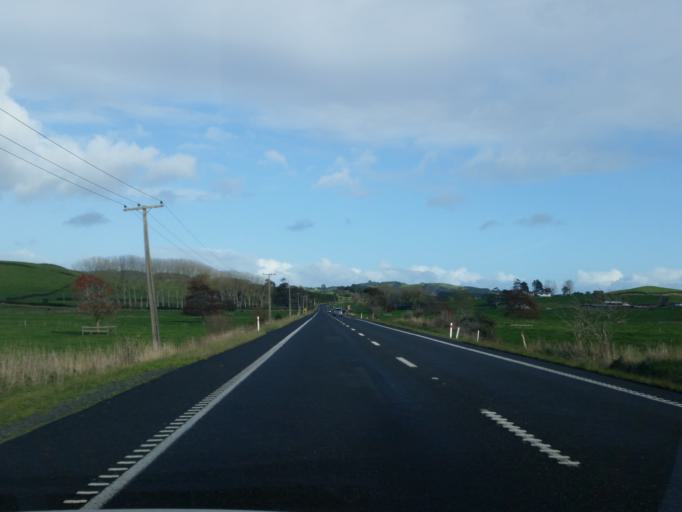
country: NZ
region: Waikato
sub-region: Hauraki District
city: Ngatea
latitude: -37.2853
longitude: 175.3944
